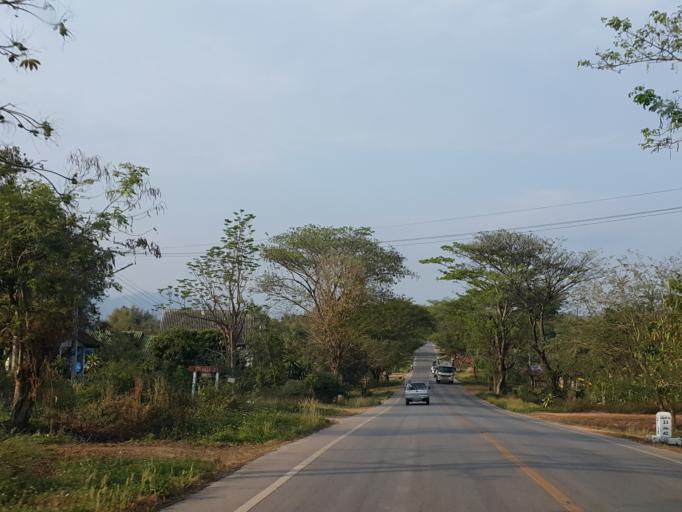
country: TH
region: Lampang
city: Chae Hom
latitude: 18.5181
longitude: 99.4763
